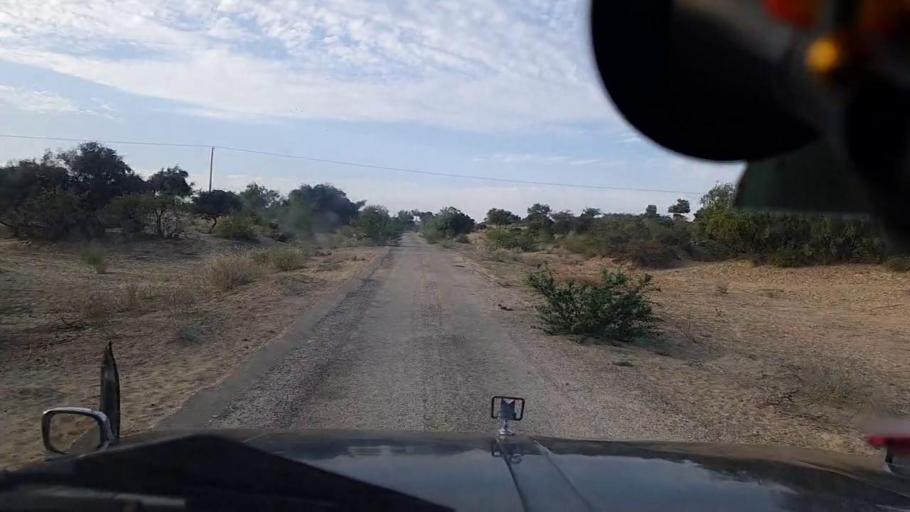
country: PK
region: Sindh
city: Diplo
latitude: 24.4664
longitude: 69.7912
